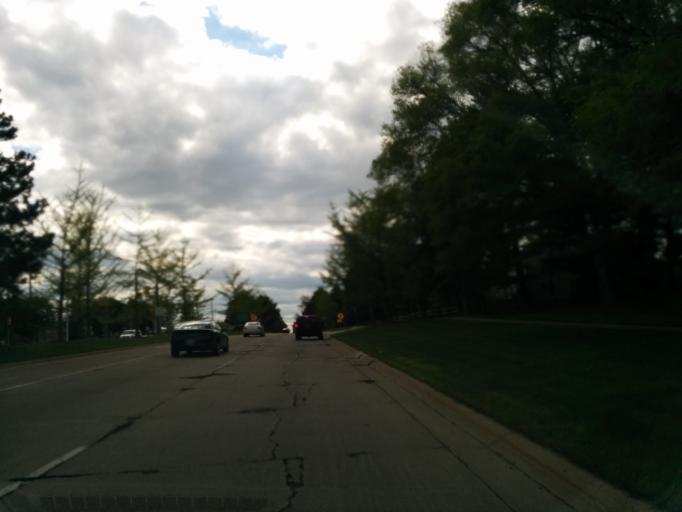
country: US
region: Michigan
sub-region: Oakland County
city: Farmington Hills
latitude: 42.4983
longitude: -83.3922
